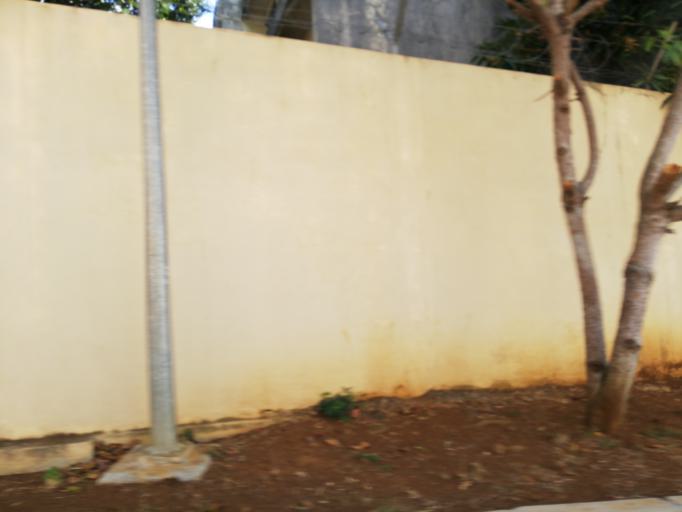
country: MU
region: Plaines Wilhems
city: Ebene
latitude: -20.2283
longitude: 57.4604
